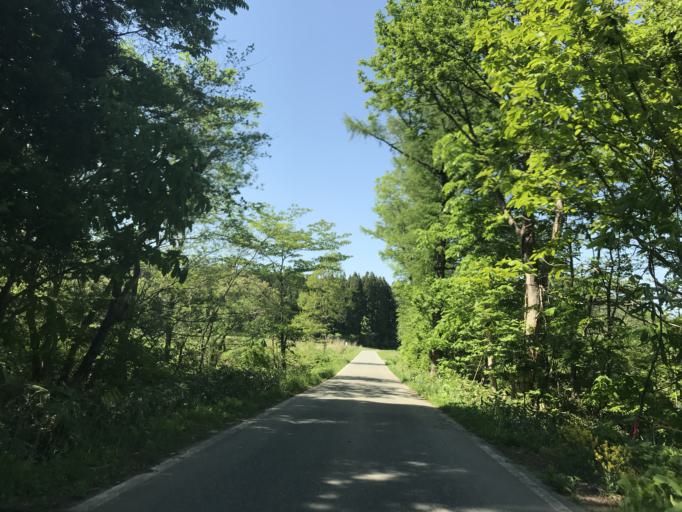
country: JP
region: Iwate
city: Shizukuishi
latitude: 39.5635
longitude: 140.8316
